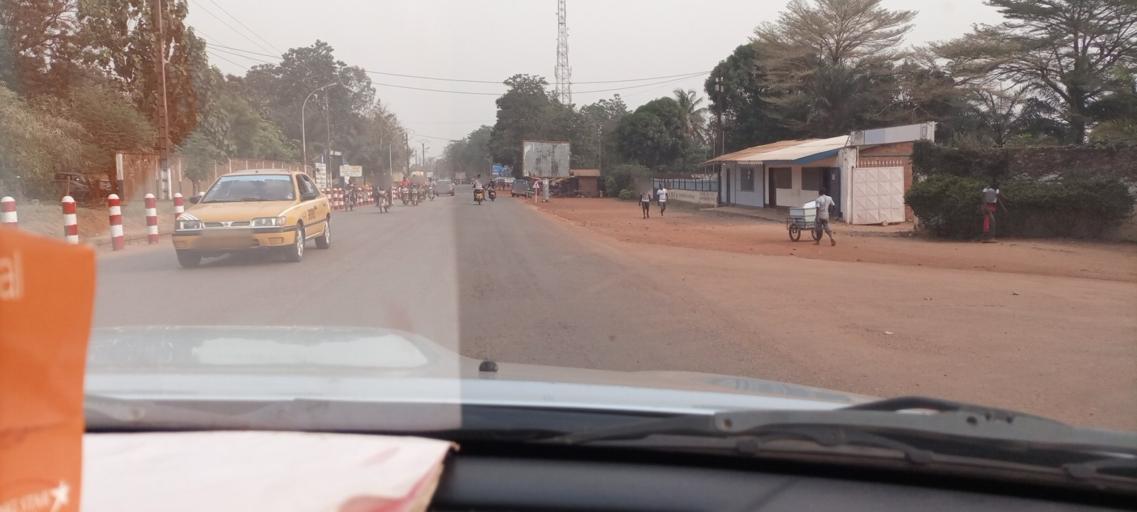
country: CF
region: Bangui
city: Bangui
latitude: 4.3763
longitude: 18.5704
